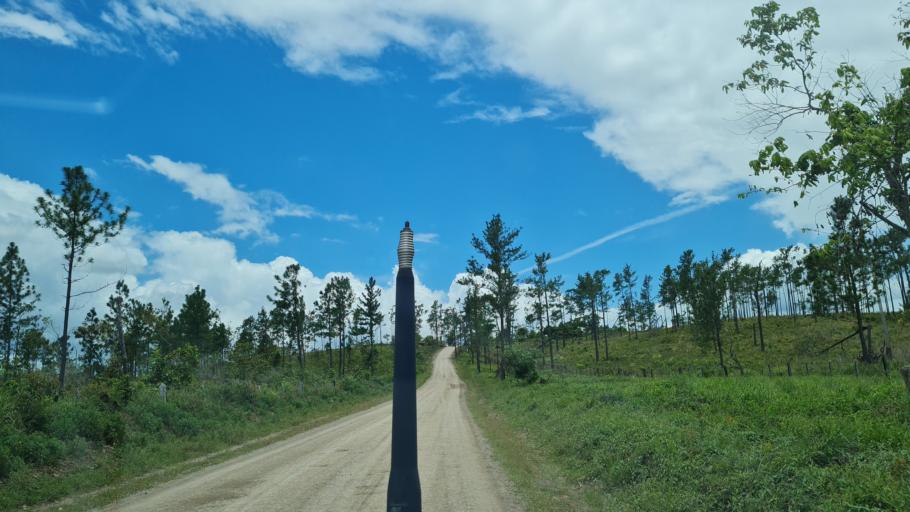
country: NI
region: Atlantico Norte (RAAN)
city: Siuna
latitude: 13.5756
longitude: -84.3237
